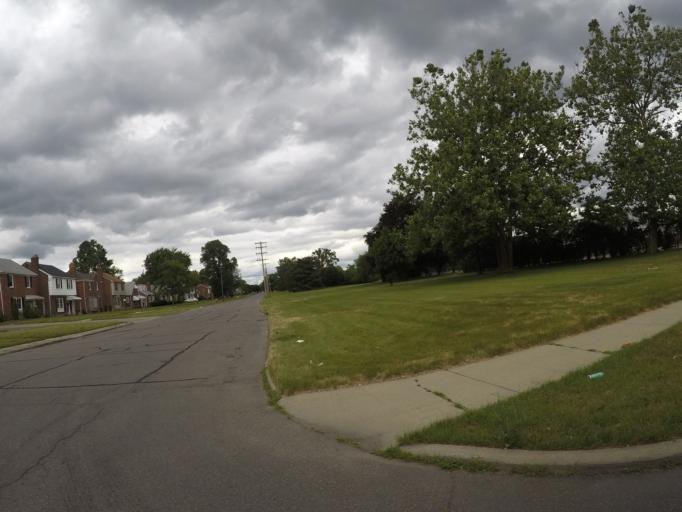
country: US
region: Michigan
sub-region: Oakland County
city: Oak Park
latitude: 42.4163
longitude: -83.1968
